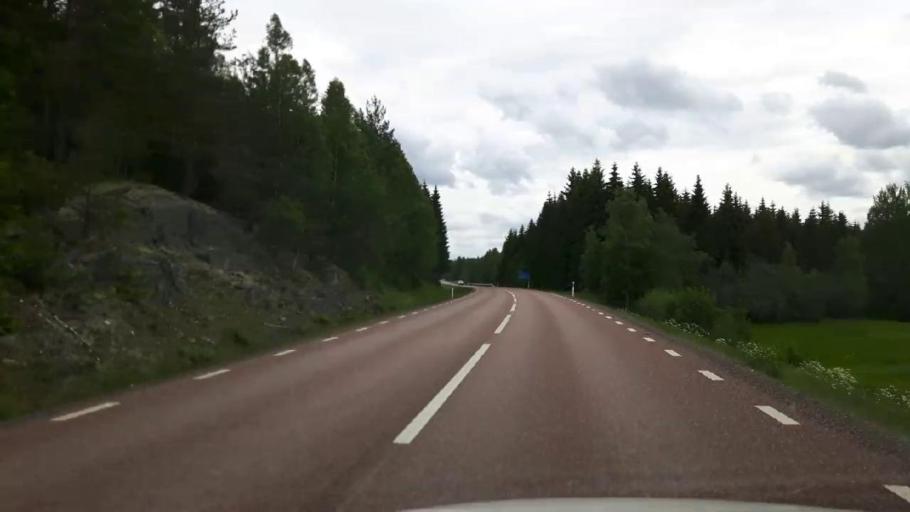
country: SE
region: Dalarna
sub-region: Hedemora Kommun
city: Brunna
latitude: 60.2087
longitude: 15.9916
